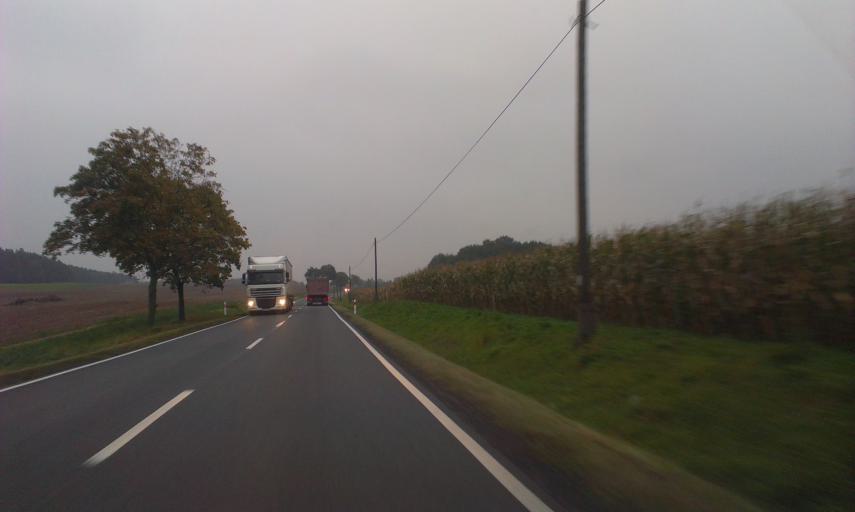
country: PL
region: Kujawsko-Pomorskie
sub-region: Powiat sepolenski
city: Sepolno Krajenskie
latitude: 53.4380
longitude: 17.6097
